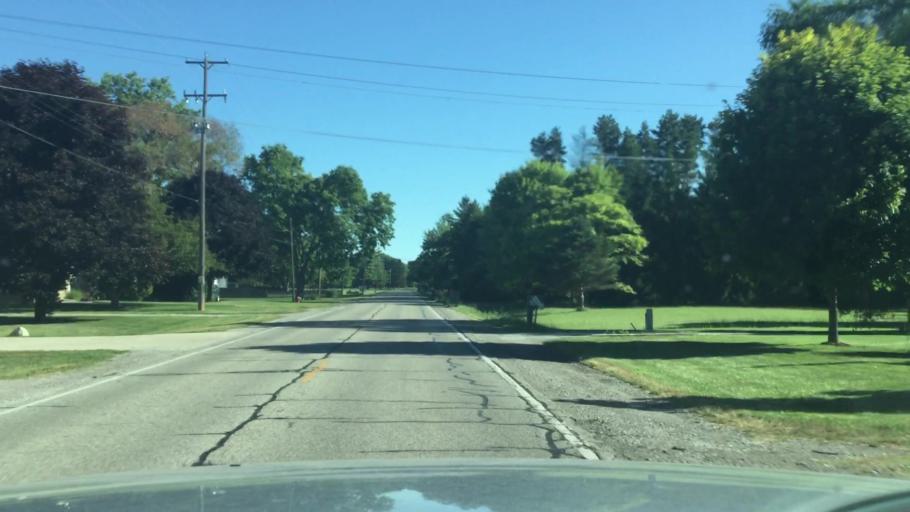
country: US
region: Michigan
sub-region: Saginaw County
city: Shields
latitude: 43.4196
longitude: -84.0520
